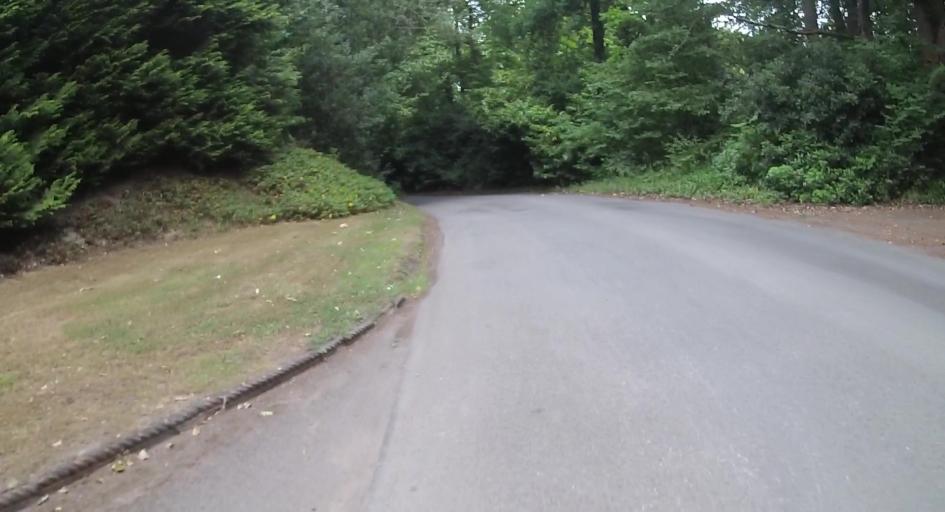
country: GB
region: England
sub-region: Surrey
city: Seale
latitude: 51.2193
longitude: -0.7328
